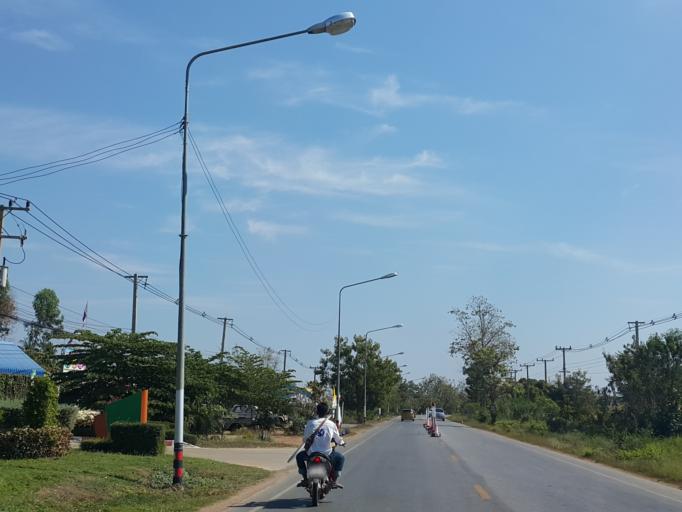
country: TH
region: Sukhothai
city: Thung Saliam
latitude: 17.3178
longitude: 99.6841
